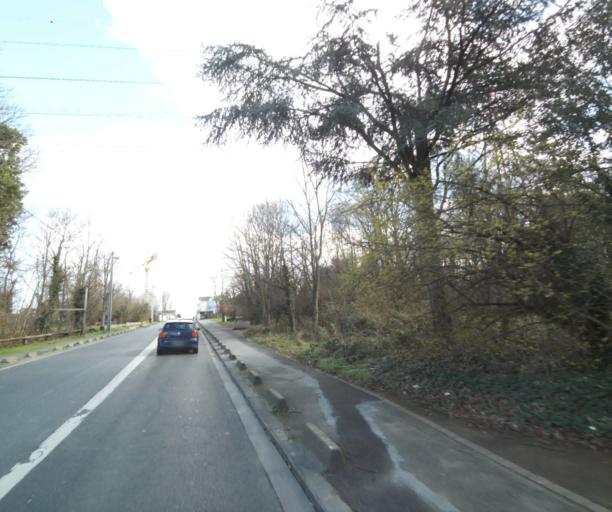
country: FR
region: Ile-de-France
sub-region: Departement du Val-d'Oise
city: Montmagny
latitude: 48.9639
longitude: 2.3501
